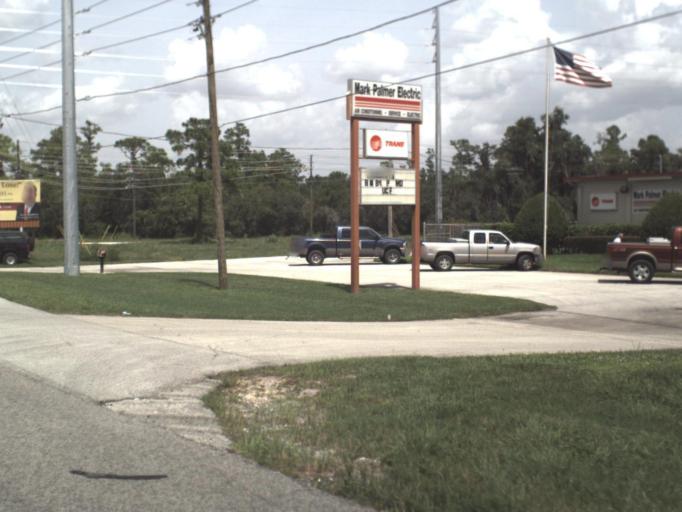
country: US
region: Florida
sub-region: Highlands County
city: Avon Park
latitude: 27.5291
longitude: -81.5001
